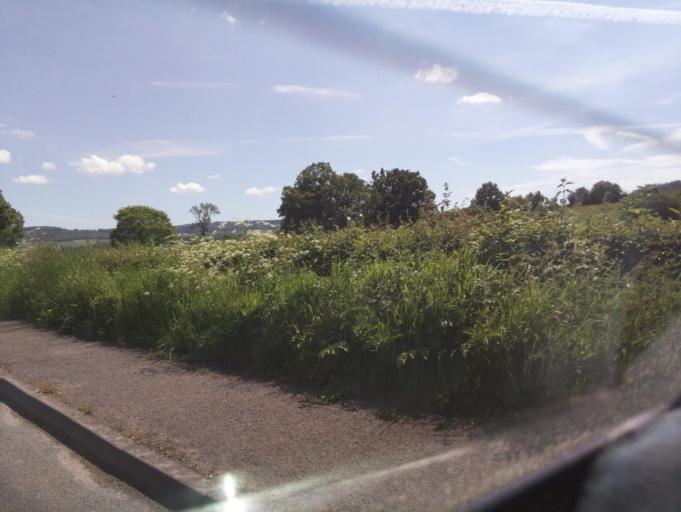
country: GB
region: Wales
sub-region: Monmouthshire
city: Monmouth
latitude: 51.8228
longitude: -2.7409
